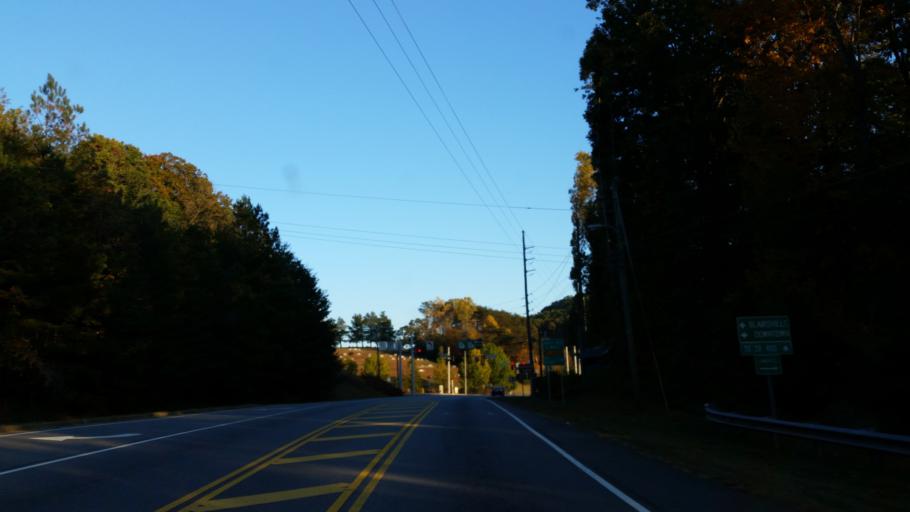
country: US
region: Georgia
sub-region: Lumpkin County
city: Dahlonega
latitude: 34.5275
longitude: -83.9923
